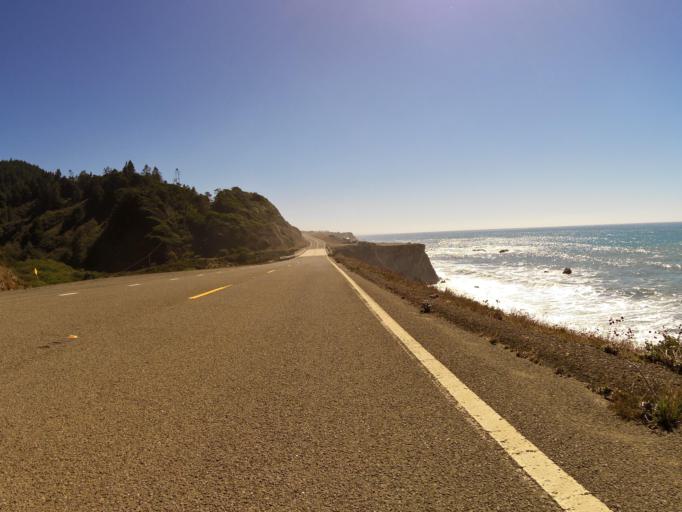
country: US
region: California
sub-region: Mendocino County
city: Fort Bragg
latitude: 39.7044
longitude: -123.8039
